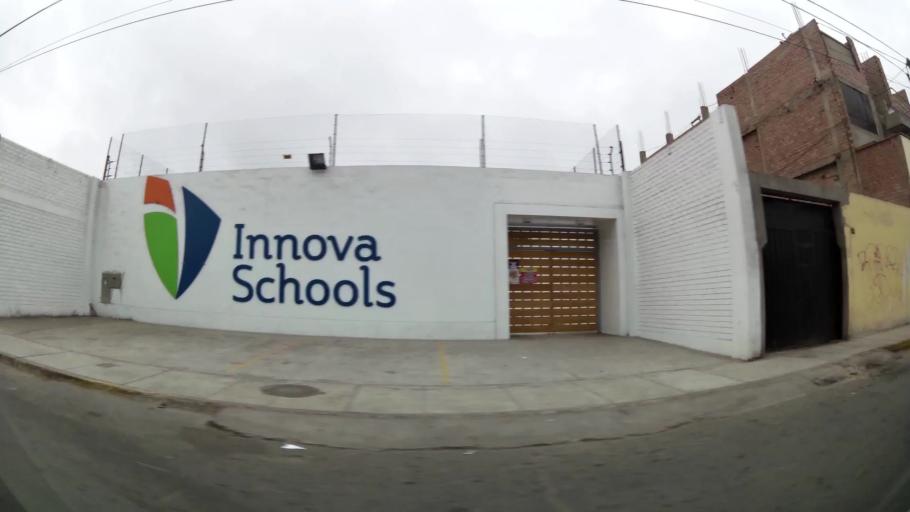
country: PE
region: Callao
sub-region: Callao
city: Callao
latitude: -12.0777
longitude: -77.1095
